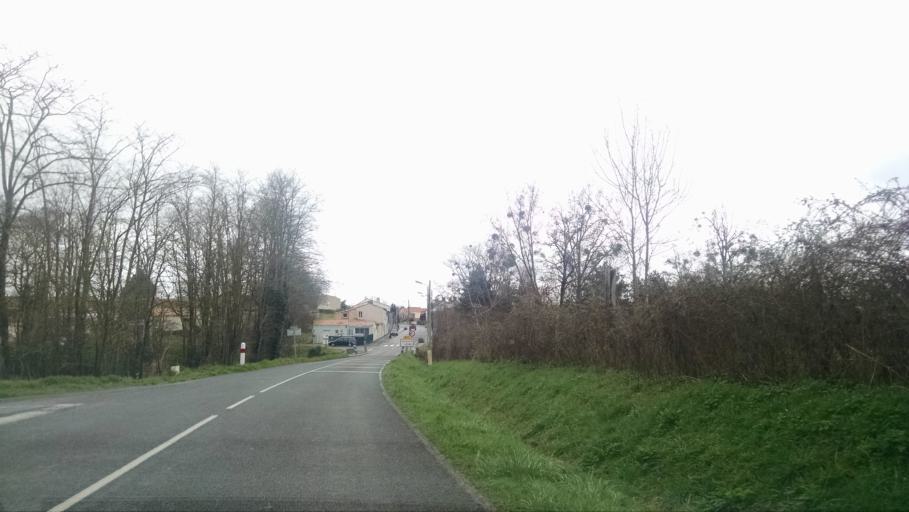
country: FR
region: Pays de la Loire
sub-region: Departement de la Loire-Atlantique
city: Maisdon-sur-Sevre
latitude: 47.0930
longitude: -1.3875
